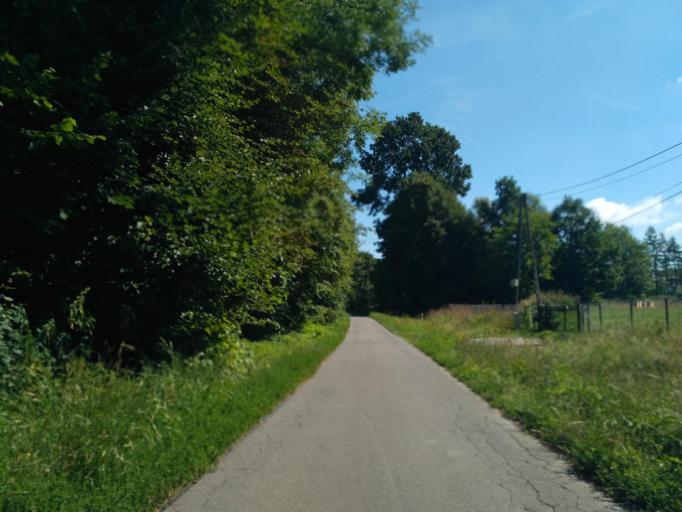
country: PL
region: Subcarpathian Voivodeship
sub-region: Powiat sanocki
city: Zarszyn
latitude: 49.6181
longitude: 22.0132
